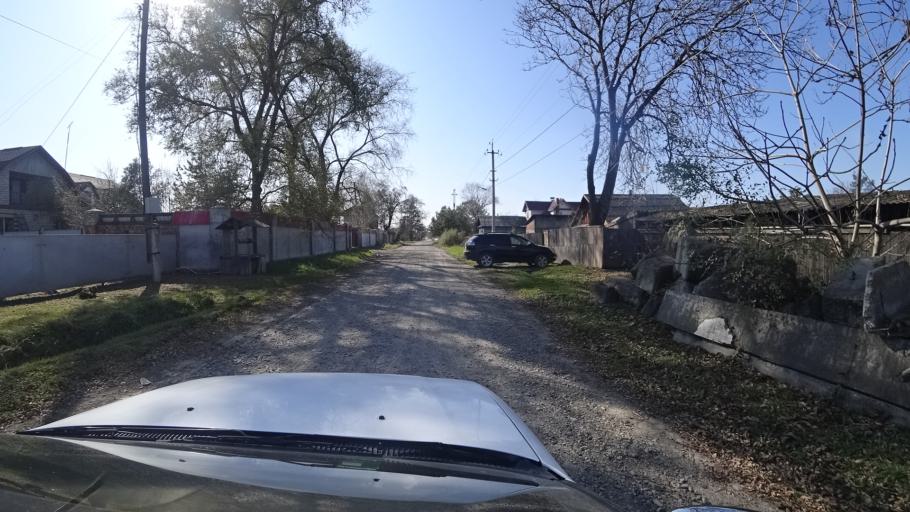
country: RU
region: Primorskiy
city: Dal'nerechensk
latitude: 45.9284
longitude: 133.7445
